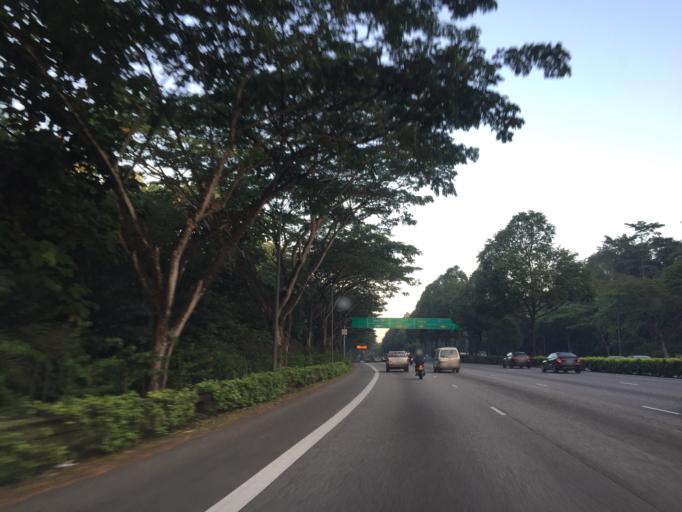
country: SG
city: Singapore
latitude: 1.3289
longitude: 103.8233
